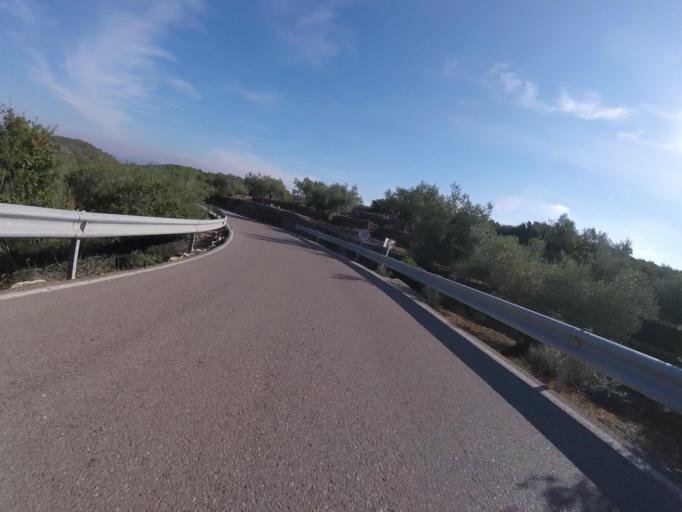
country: ES
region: Valencia
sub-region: Provincia de Castello
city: Benlloch
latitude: 40.2419
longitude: 0.0770
